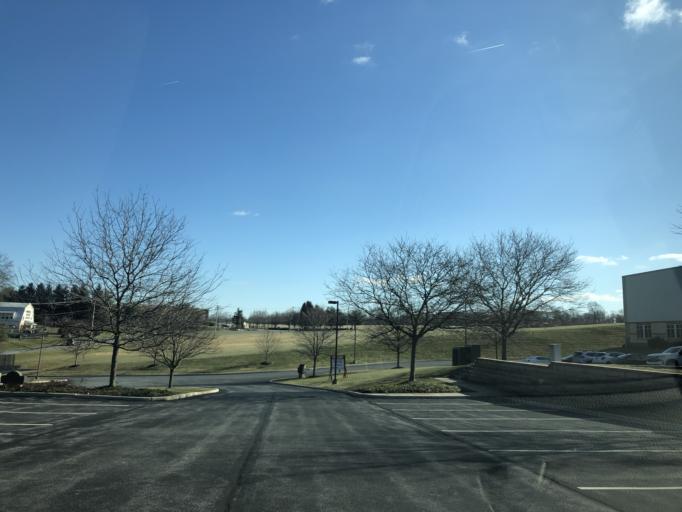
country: US
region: Pennsylvania
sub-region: Chester County
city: Coatesville
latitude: 39.9927
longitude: -75.8758
